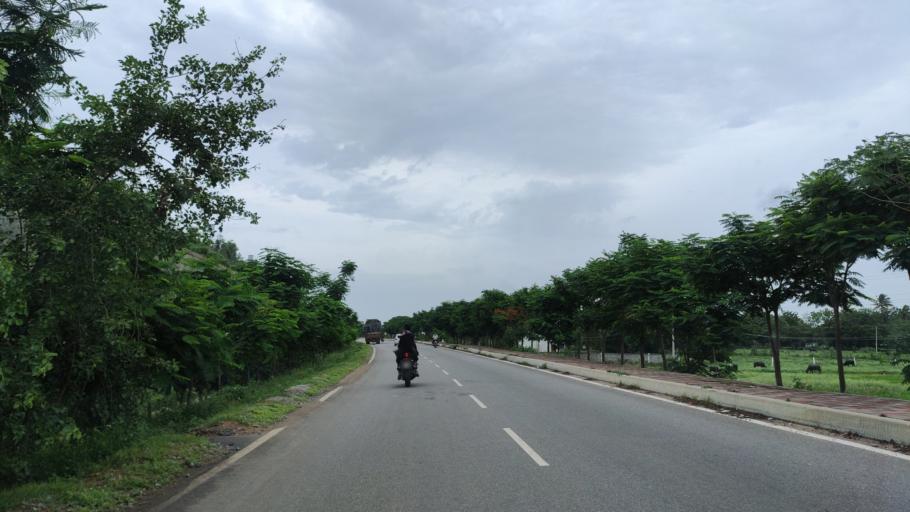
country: IN
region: Telangana
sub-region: Rangareddi
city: Secunderabad
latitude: 17.5795
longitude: 78.5928
